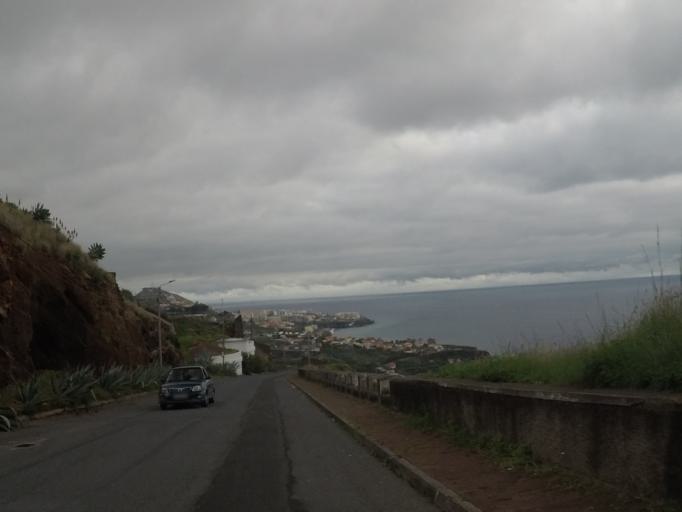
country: PT
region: Madeira
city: Camara de Lobos
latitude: 32.6518
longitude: -16.9742
